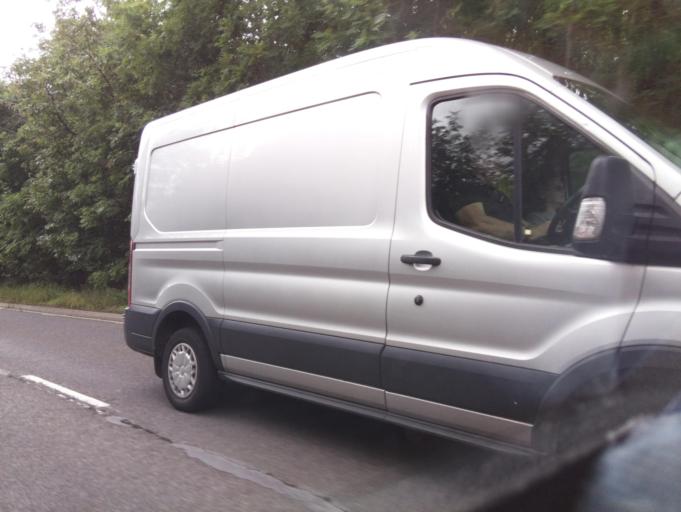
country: GB
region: England
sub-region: Northamptonshire
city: Geddington
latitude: 52.4509
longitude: -0.7362
